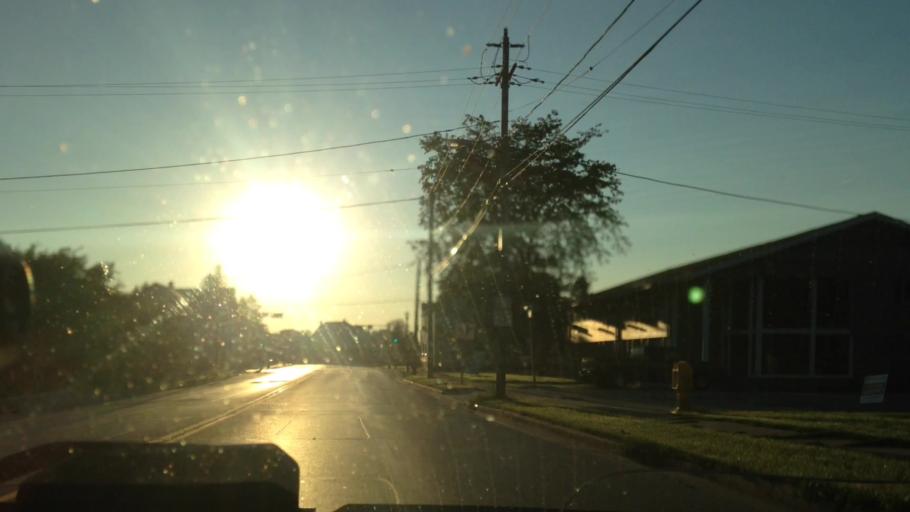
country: US
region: Wisconsin
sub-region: Ozaukee County
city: Saukville
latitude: 43.3818
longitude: -87.9414
